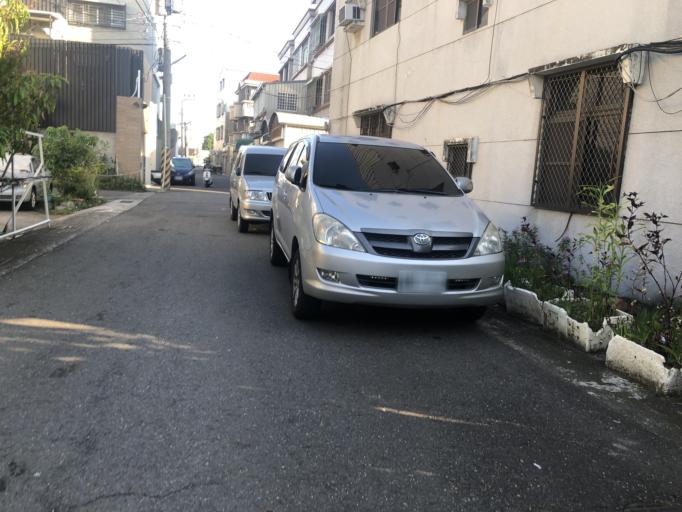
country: TW
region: Taiwan
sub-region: Tainan
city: Tainan
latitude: 23.0388
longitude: 120.1837
